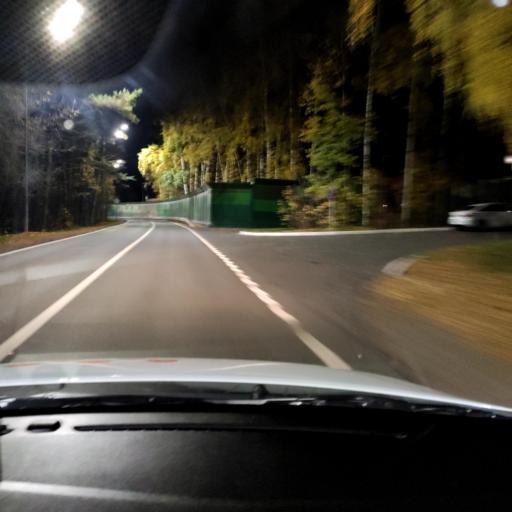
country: RU
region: Tatarstan
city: Verkhniy Uslon
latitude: 55.6300
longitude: 49.0154
